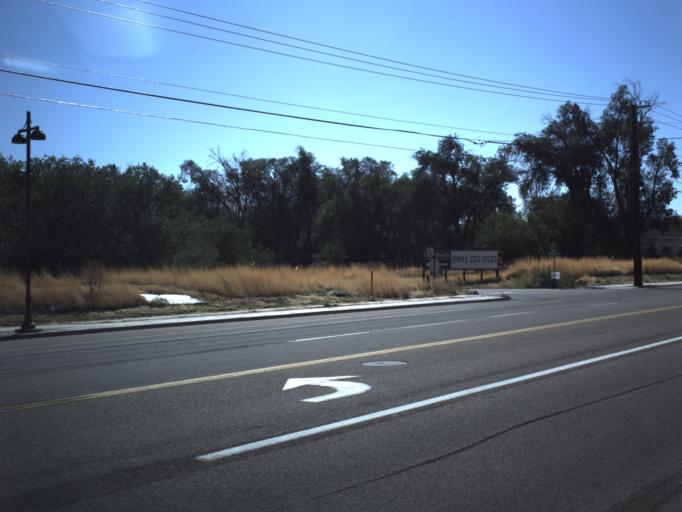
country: US
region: Utah
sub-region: Salt Lake County
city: Bluffdale
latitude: 40.4978
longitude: -111.9387
